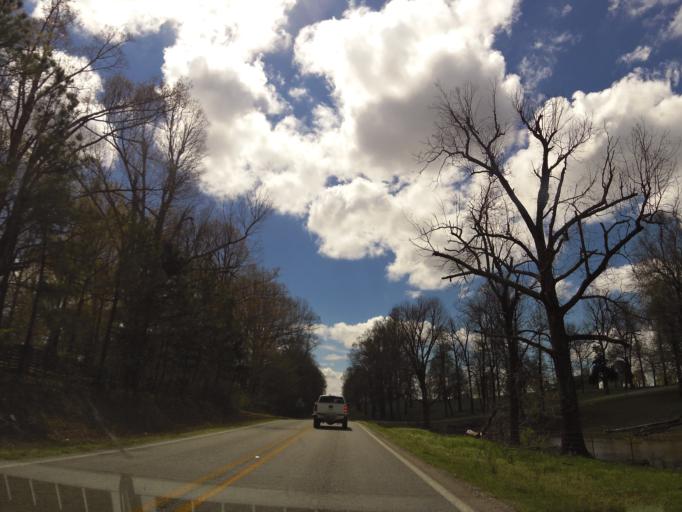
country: US
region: Arkansas
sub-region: Craighead County
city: Bono
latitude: 35.9989
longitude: -90.7091
